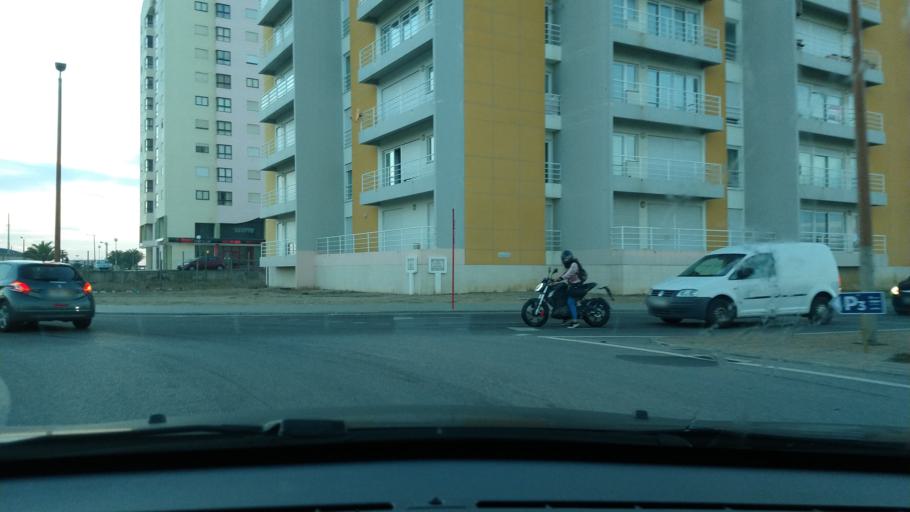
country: PT
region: Leiria
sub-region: Peniche
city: Peniche
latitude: 39.3586
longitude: -9.3661
